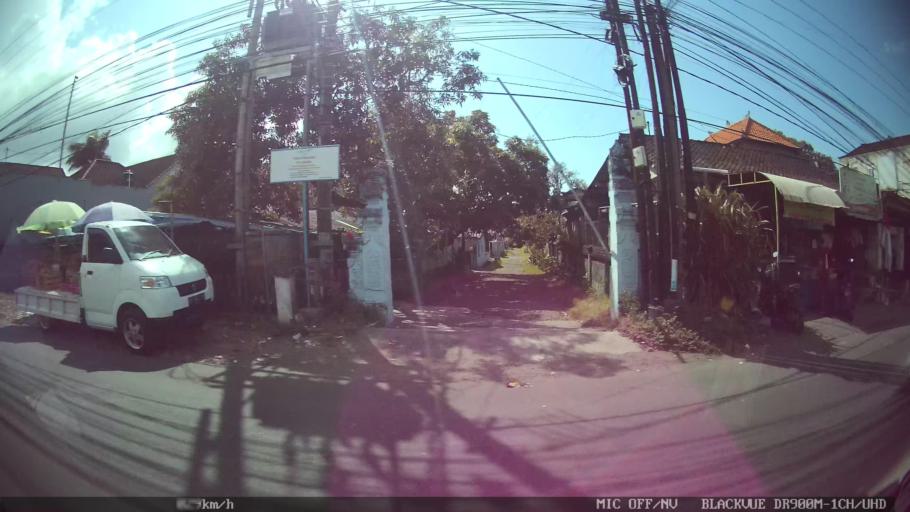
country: ID
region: Bali
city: Karyadharma
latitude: -8.7125
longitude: 115.2000
